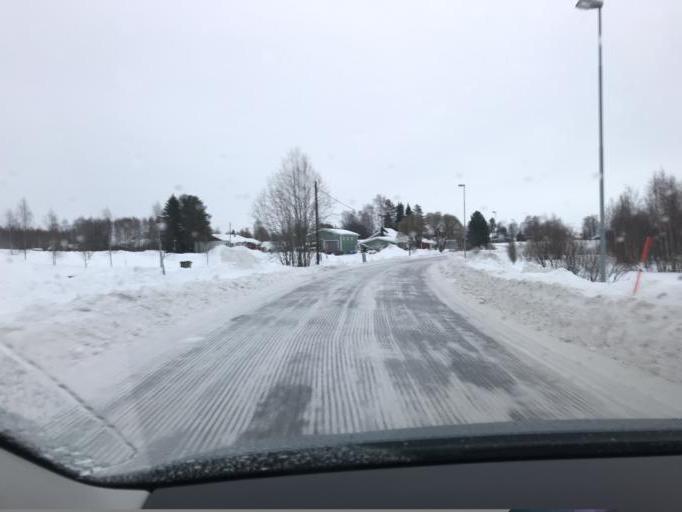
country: SE
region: Norrbotten
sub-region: Lulea Kommun
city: Sodra Sunderbyn
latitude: 65.6629
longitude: 21.9291
